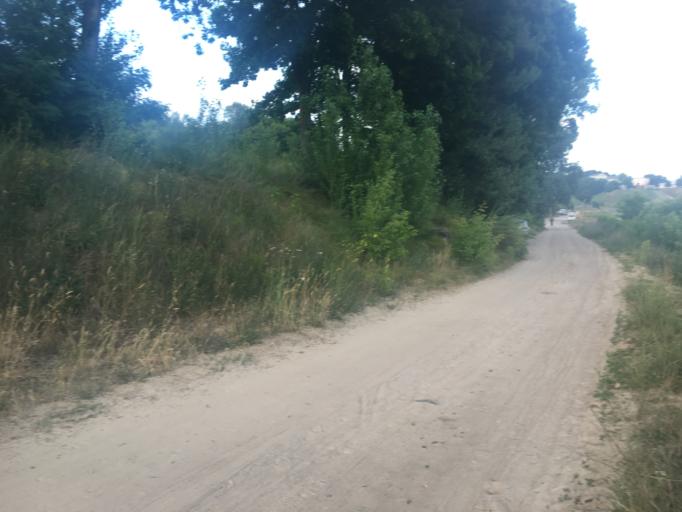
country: BY
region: Grodnenskaya
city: Hrodna
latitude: 53.6791
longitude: 23.8102
